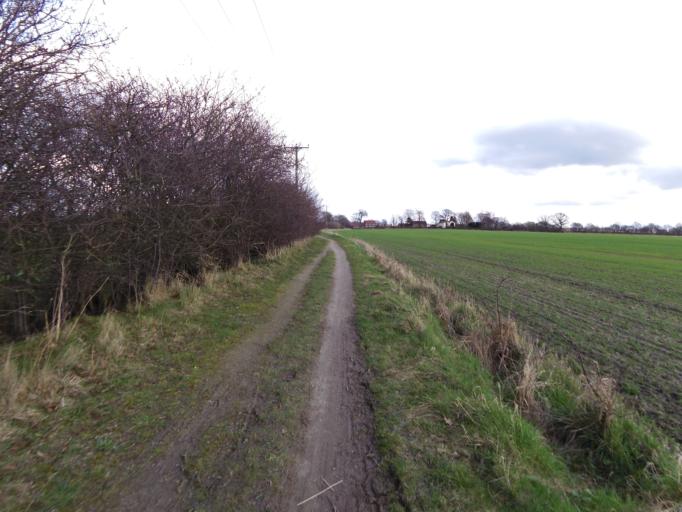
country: GB
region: England
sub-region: East Riding of Yorkshire
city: Pollington
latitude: 53.6574
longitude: -1.0637
